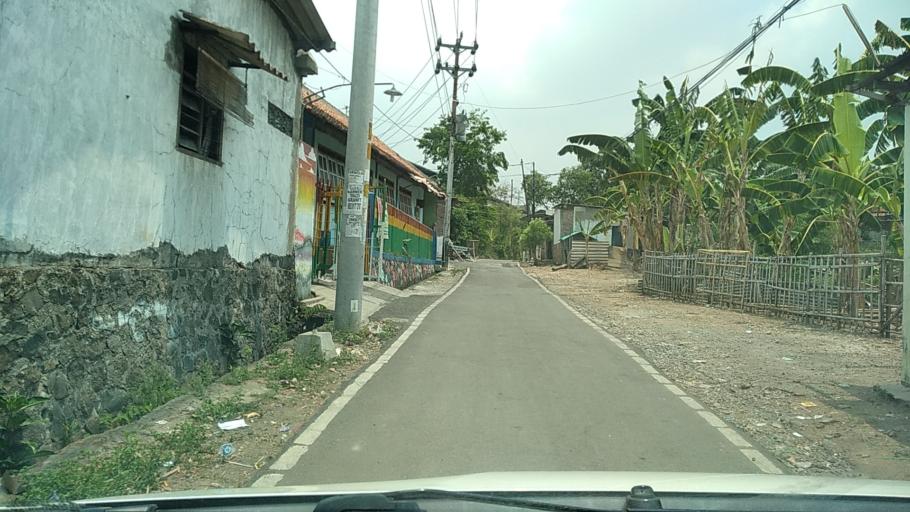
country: ID
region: Central Java
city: Semarang
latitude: -6.9901
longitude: 110.3625
